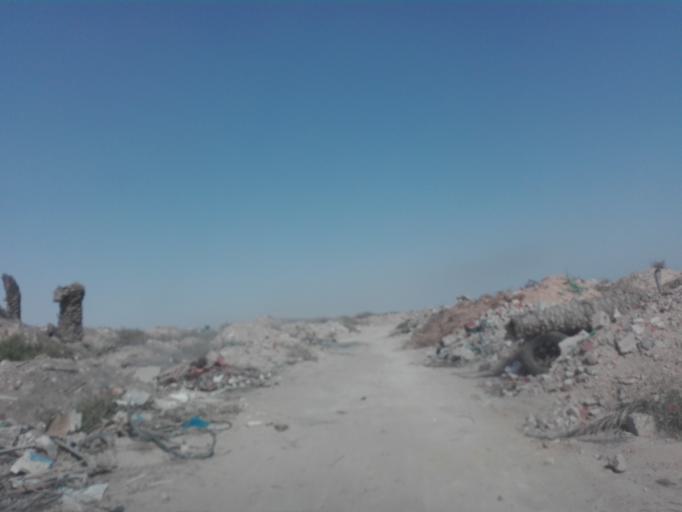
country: TN
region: Qabis
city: Gabes
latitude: 33.9620
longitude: 10.0661
